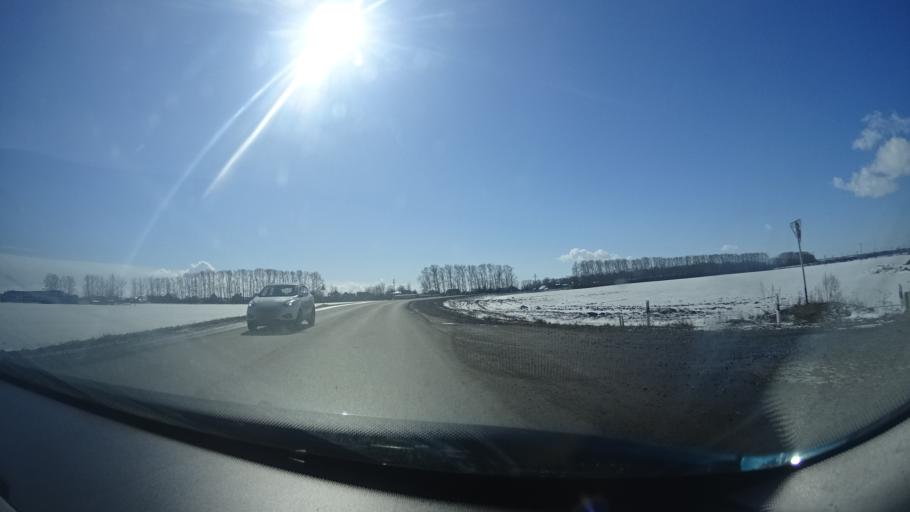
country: RU
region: Bashkortostan
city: Ufa
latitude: 54.6152
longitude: 55.8911
